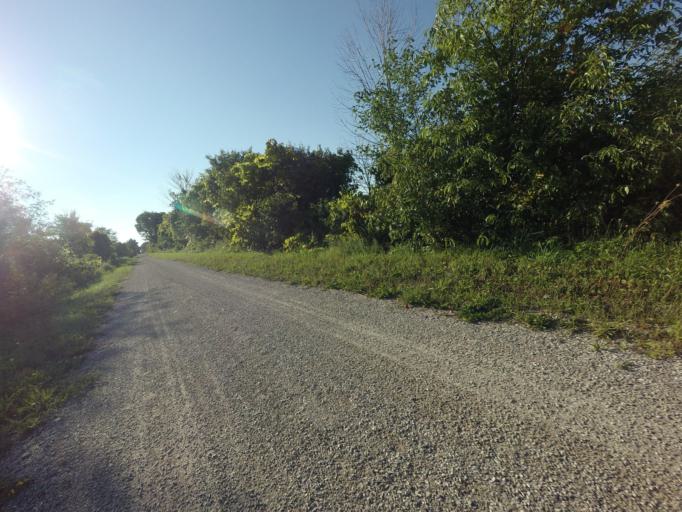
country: CA
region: Ontario
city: Goderich
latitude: 43.7518
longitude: -81.5885
